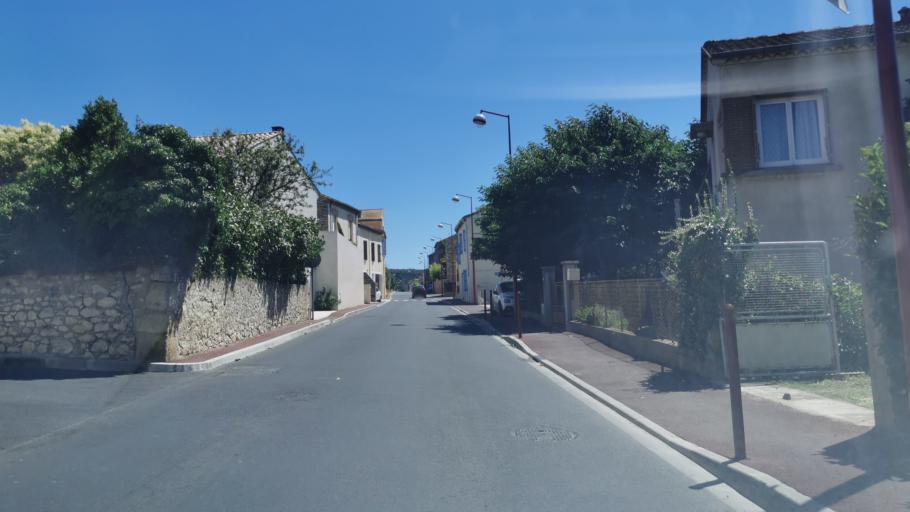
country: FR
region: Languedoc-Roussillon
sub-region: Departement de l'Aude
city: Vinassan
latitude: 43.2024
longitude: 3.0744
